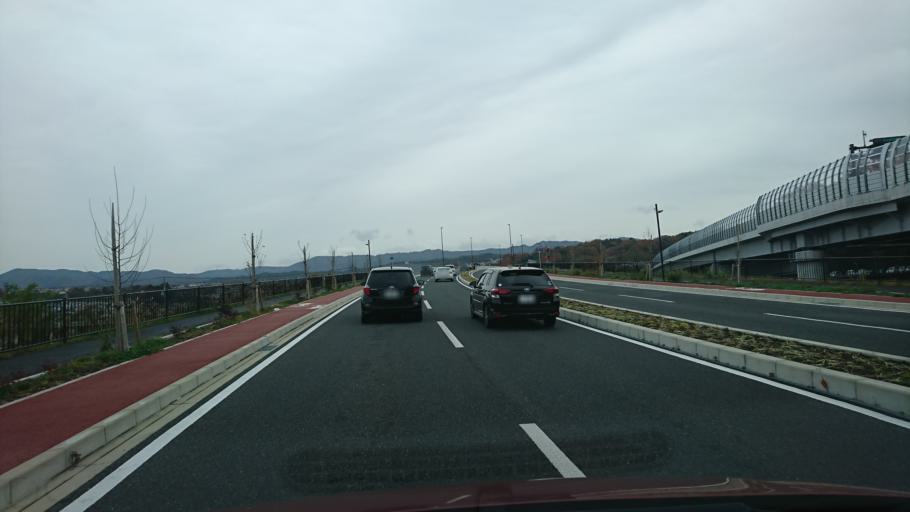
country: JP
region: Osaka
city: Ikeda
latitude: 34.8849
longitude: 135.4017
